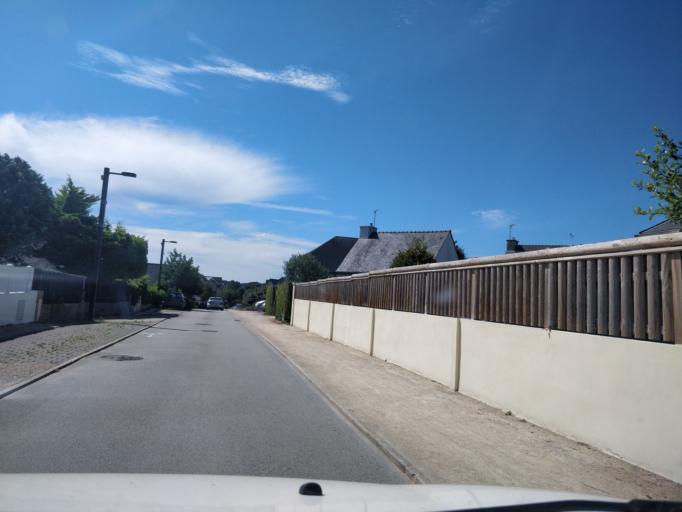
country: FR
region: Brittany
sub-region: Departement du Morbihan
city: Saint-Philibert
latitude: 47.5884
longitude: -3.0010
